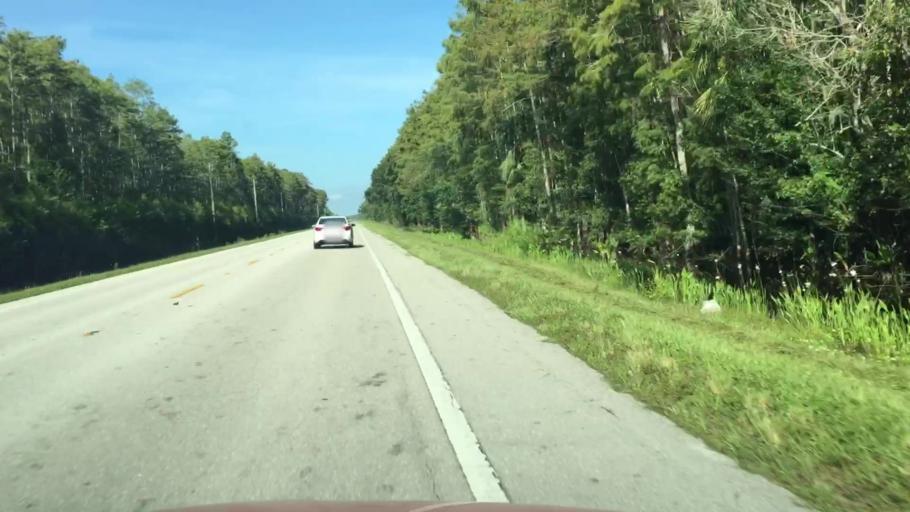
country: US
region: Florida
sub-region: Collier County
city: Immokalee
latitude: 26.3673
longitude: -81.4472
